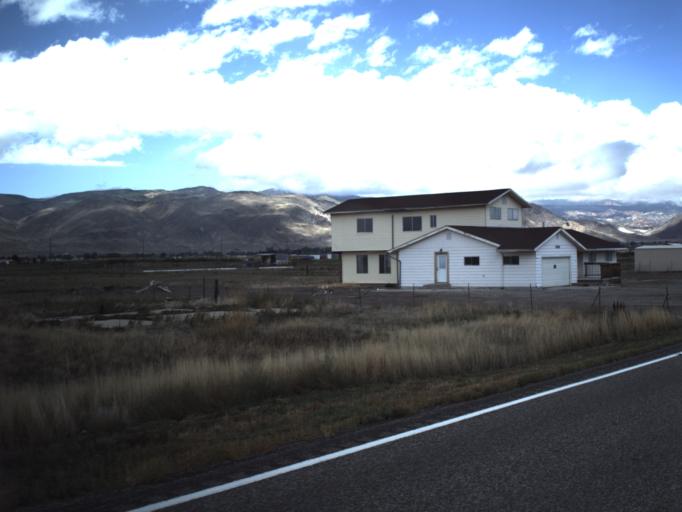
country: US
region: Utah
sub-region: Sevier County
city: Monroe
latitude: 38.6552
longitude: -112.1215
